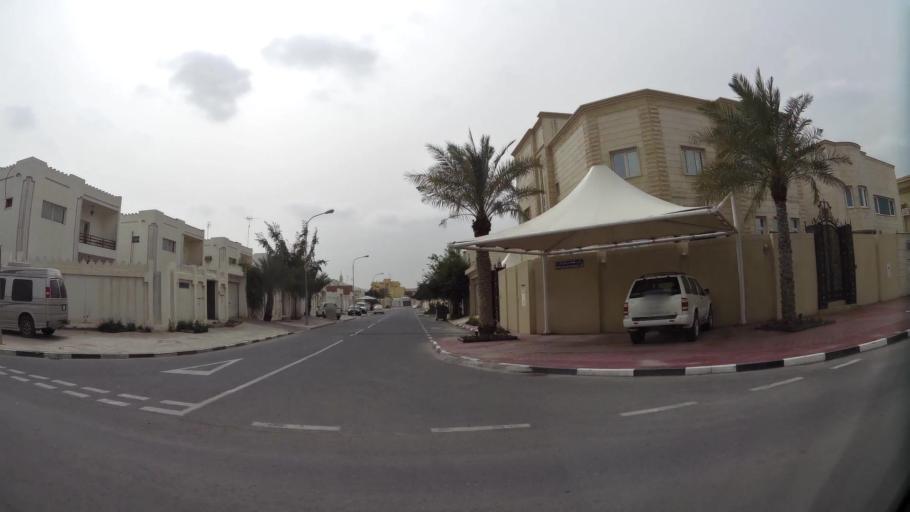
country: QA
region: Baladiyat ad Dawhah
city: Doha
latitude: 25.2483
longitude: 51.5280
